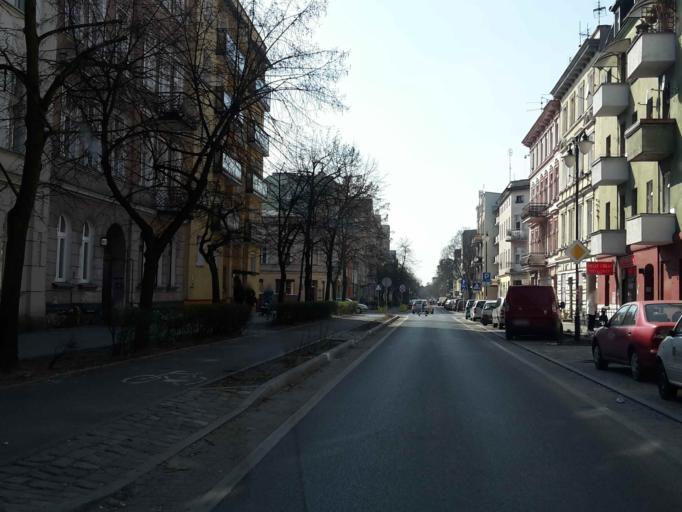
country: PL
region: Kujawsko-Pomorskie
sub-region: Torun
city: Torun
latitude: 53.0118
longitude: 18.5759
